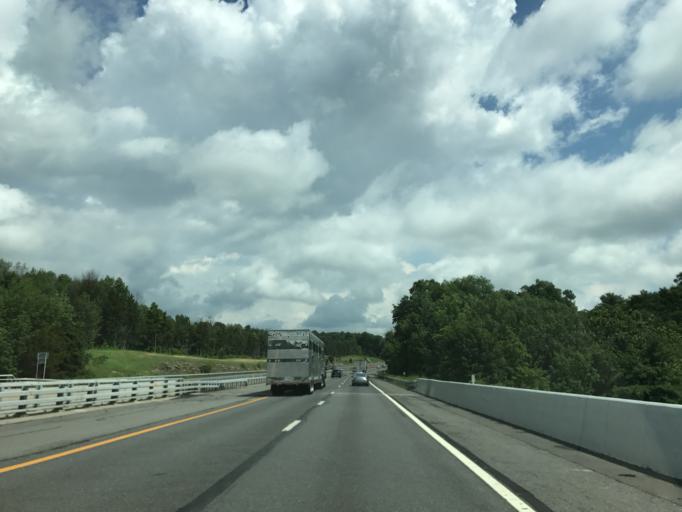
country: US
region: New York
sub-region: Greene County
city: Jefferson Heights
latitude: 42.2180
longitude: -73.9143
